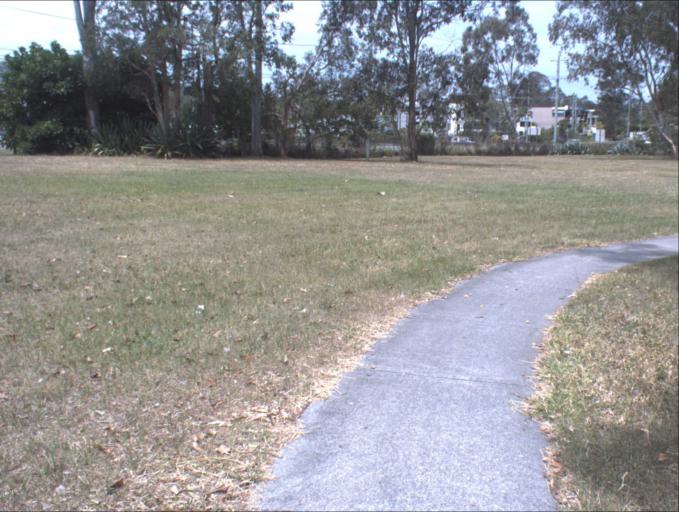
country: AU
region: Queensland
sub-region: Logan
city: Slacks Creek
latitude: -27.6657
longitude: 153.1731
